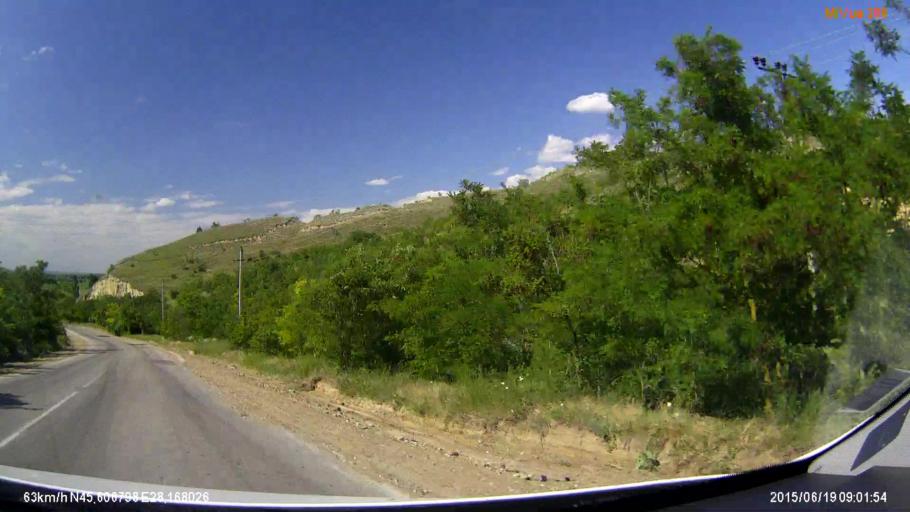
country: RO
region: Galati
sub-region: Comuna Tulucesti
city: Sivita
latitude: 45.6066
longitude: 28.1681
